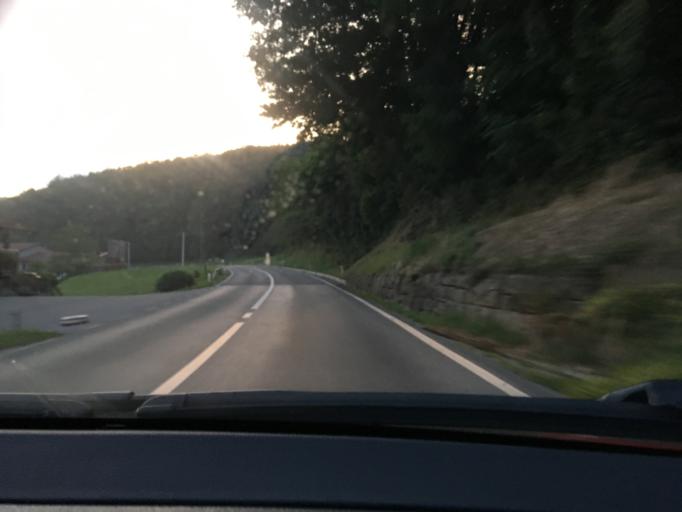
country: SI
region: Pivka
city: Pivka
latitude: 45.6187
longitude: 14.1731
